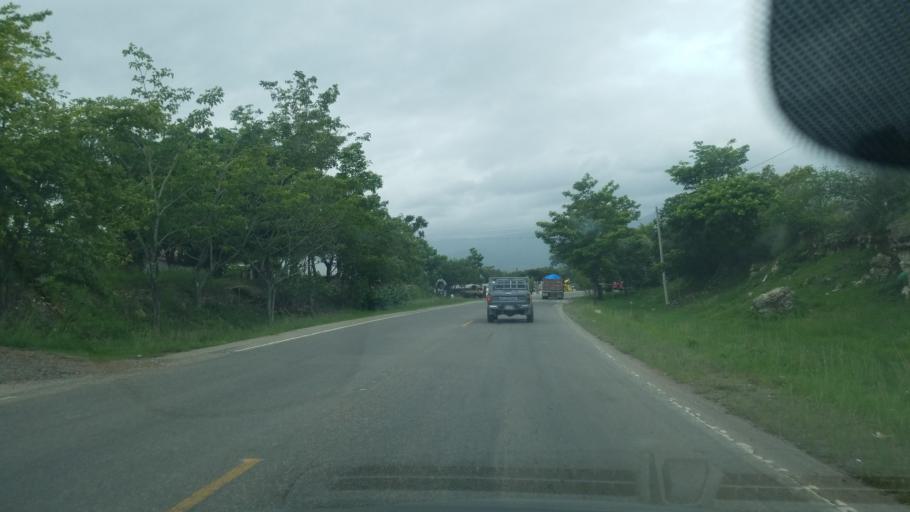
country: HN
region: Ocotepeque
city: Sensenti
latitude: 14.5129
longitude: -88.9531
